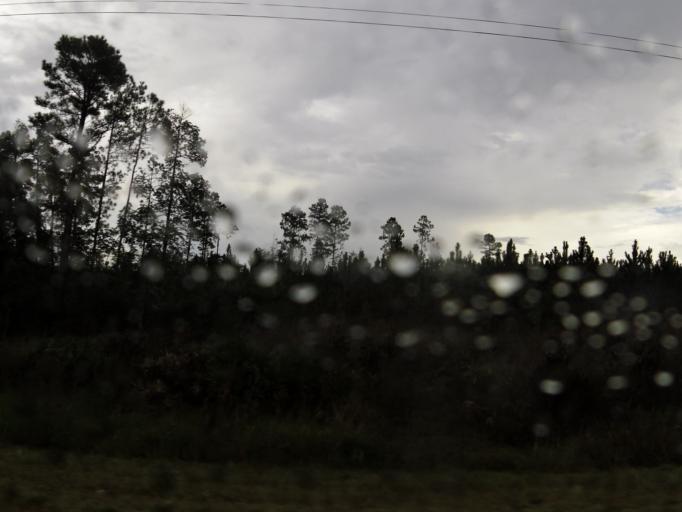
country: US
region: Florida
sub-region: Baker County
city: Macclenny
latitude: 30.4452
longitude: -82.0774
